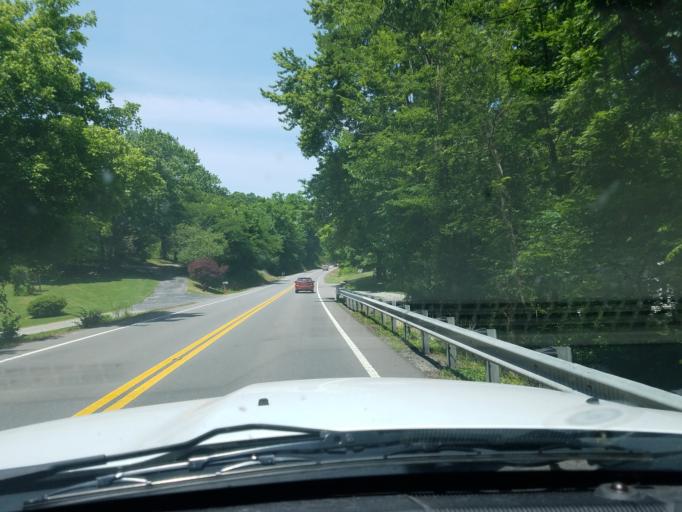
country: US
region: Tennessee
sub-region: Sumner County
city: Westmoreland
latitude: 36.4775
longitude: -86.2712
